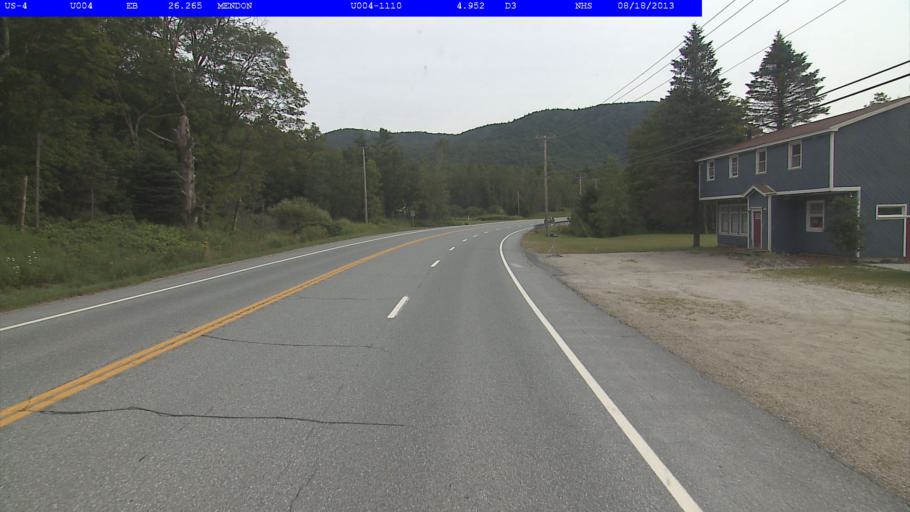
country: US
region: Vermont
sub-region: Rutland County
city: Rutland
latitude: 43.6645
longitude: -72.8638
